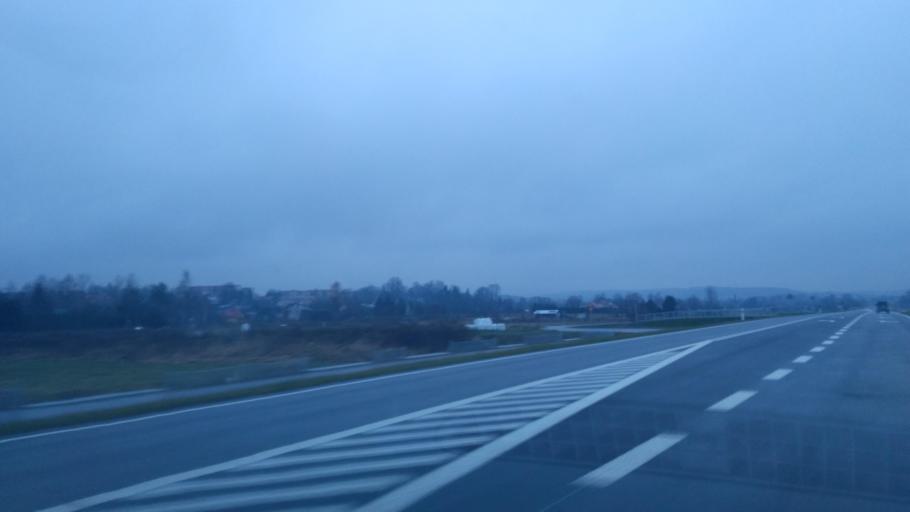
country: PL
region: Subcarpathian Voivodeship
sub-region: Powiat rzeszowski
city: Dynow
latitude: 49.8135
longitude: 22.2405
